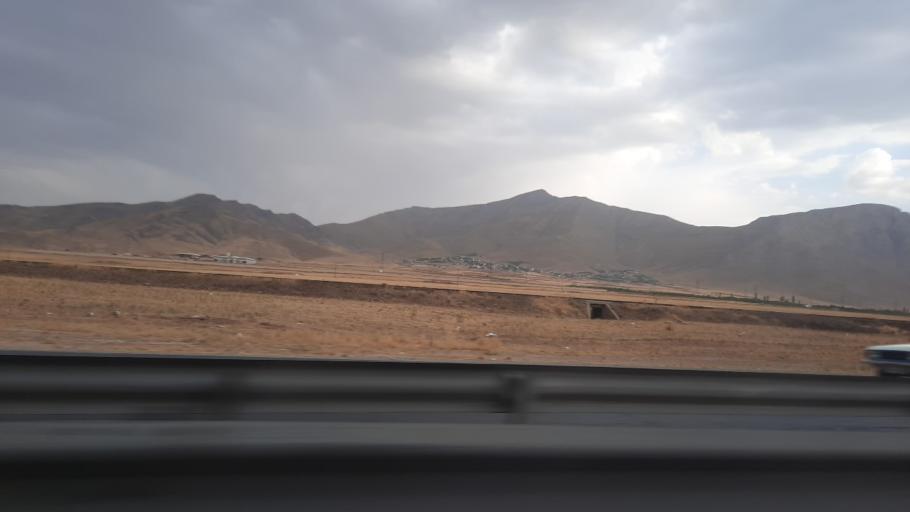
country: IR
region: Markazi
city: Arak
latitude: 34.0224
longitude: 49.5788
